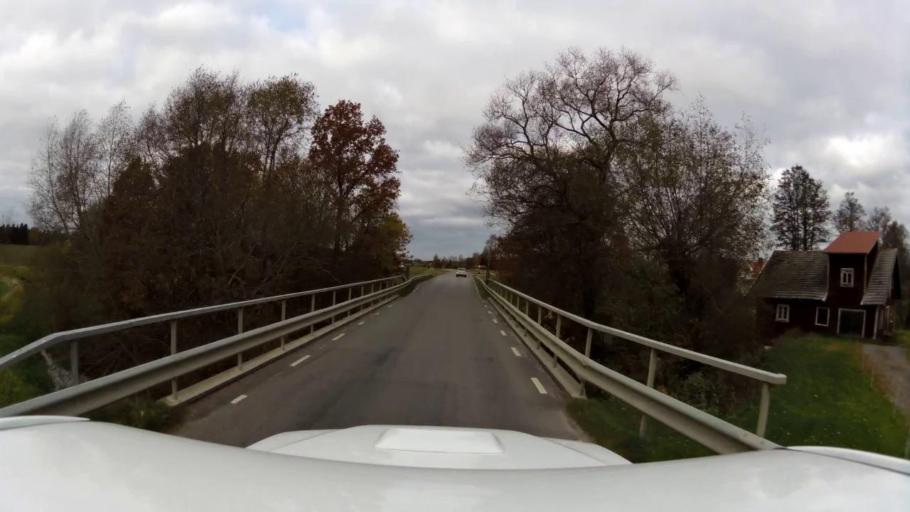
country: SE
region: OEstergoetland
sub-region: Linkopings Kommun
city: Linghem
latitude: 58.4207
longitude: 15.7317
